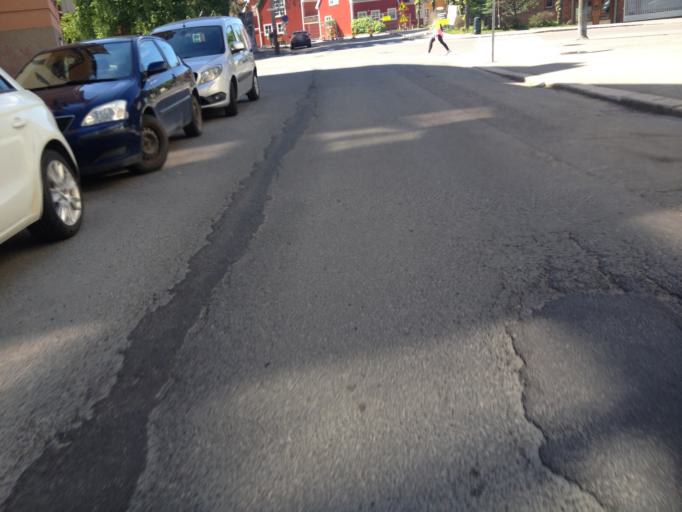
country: NO
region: Oslo
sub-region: Oslo
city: Oslo
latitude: 59.9358
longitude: 10.7631
